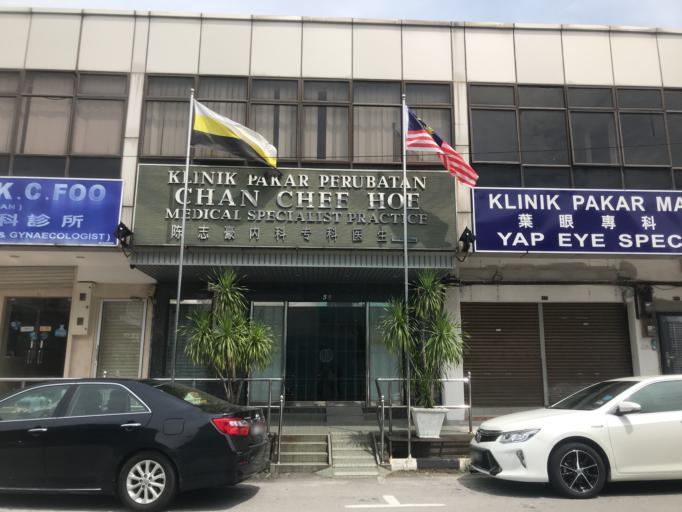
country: MY
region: Perak
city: Ipoh
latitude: 4.6063
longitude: 101.1191
